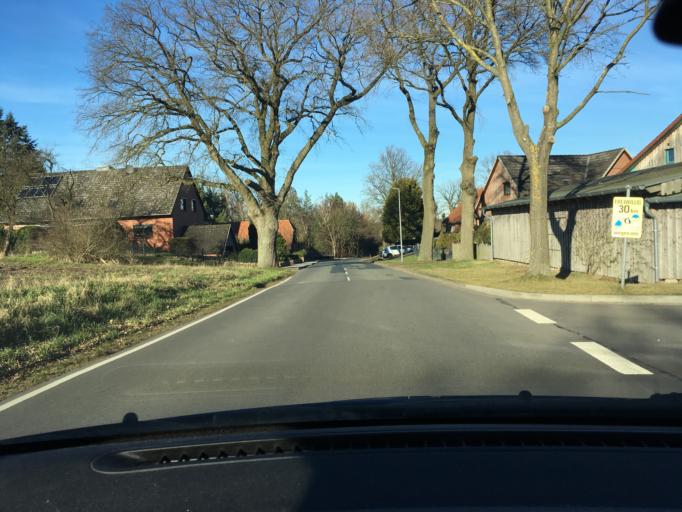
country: DE
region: Lower Saxony
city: Barnstedt
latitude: 53.1553
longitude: 10.3802
